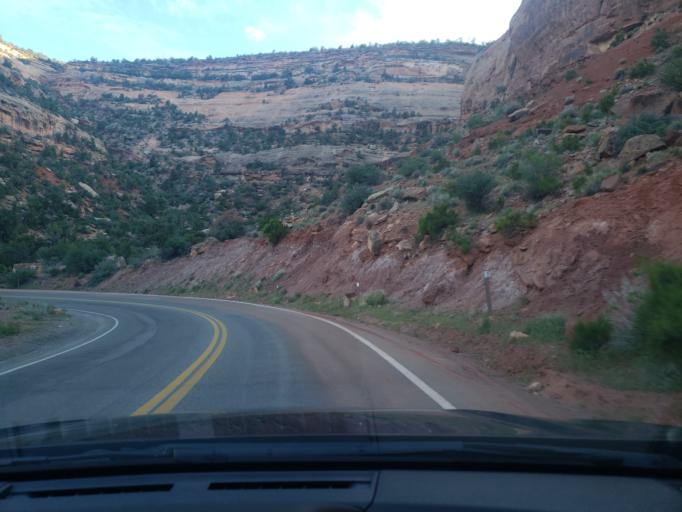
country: US
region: Colorado
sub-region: Mesa County
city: Fruita
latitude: 39.1087
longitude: -108.7365
